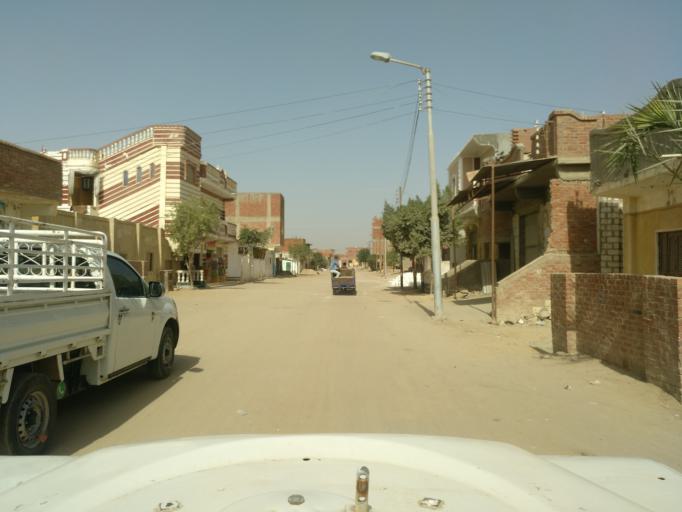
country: EG
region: Al Buhayrah
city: Beheira
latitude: 30.3814
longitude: 30.3442
